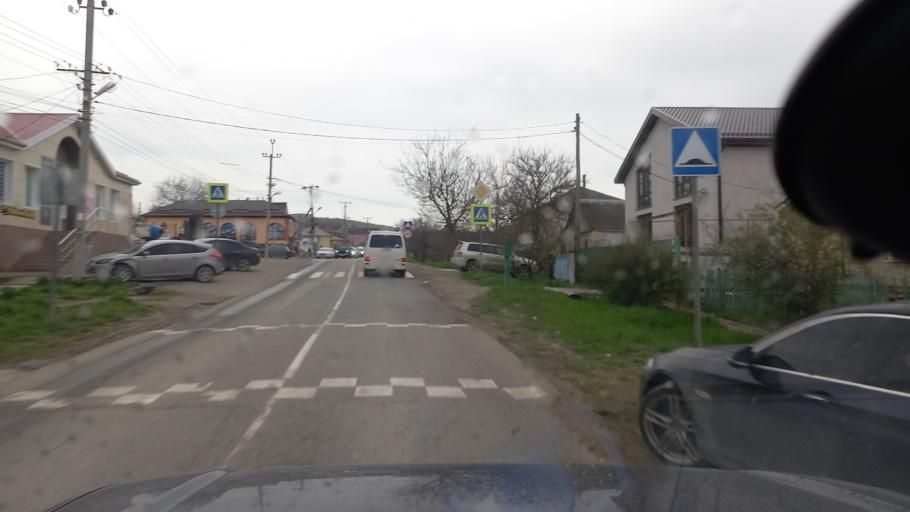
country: RU
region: Krasnodarskiy
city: Sukko
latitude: 44.8548
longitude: 37.4369
